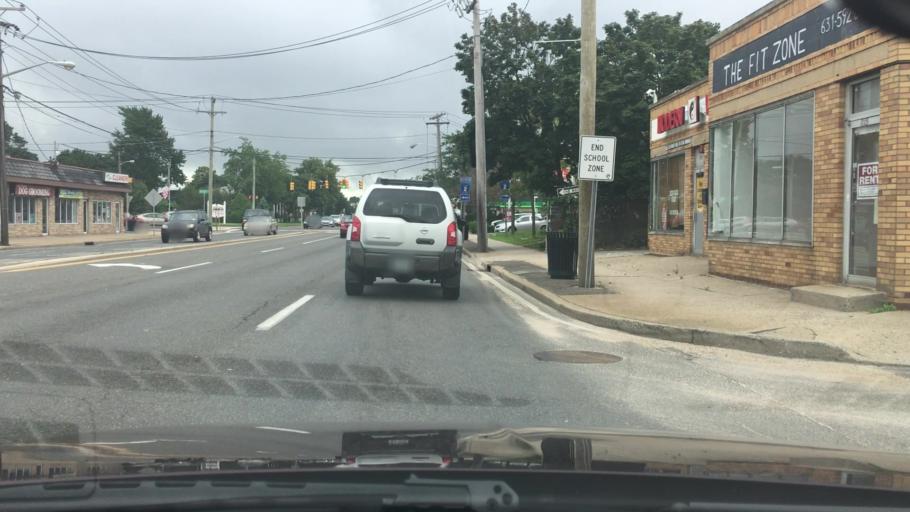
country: US
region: New York
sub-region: Suffolk County
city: North Lindenhurst
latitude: 40.7053
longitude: -73.3877
